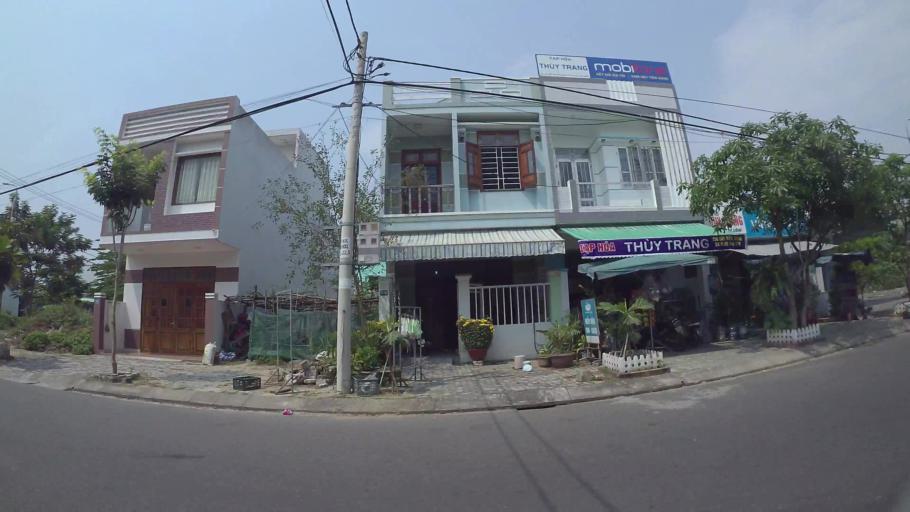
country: VN
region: Da Nang
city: Cam Le
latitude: 15.9929
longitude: 108.2135
